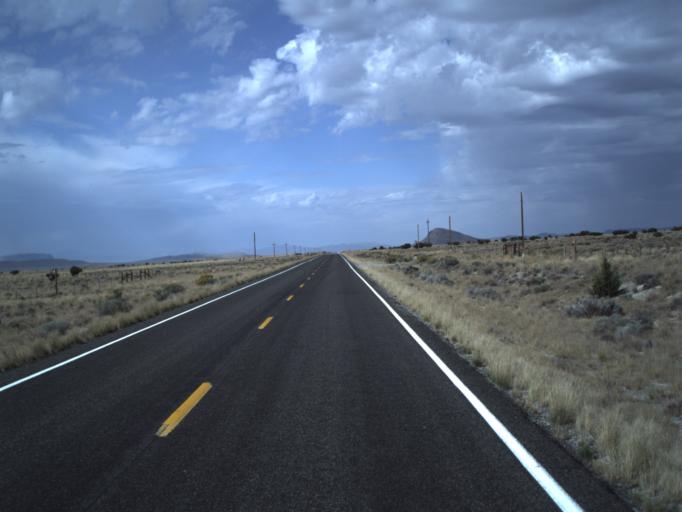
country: US
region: Utah
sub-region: Tooele County
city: Wendover
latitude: 41.4374
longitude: -113.7378
